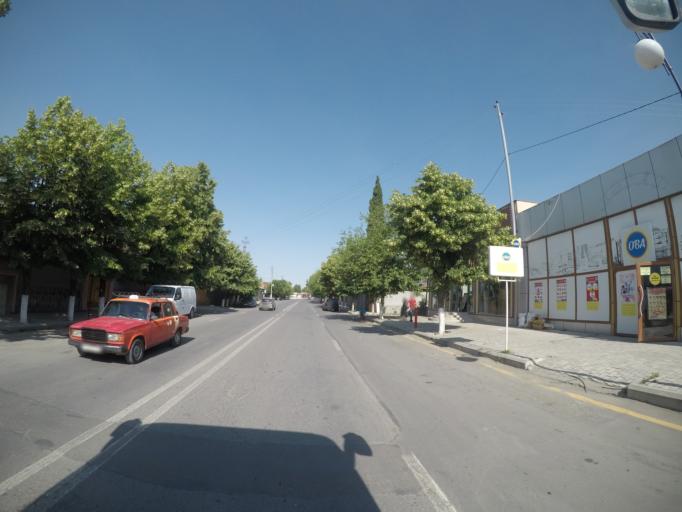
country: AZ
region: Shaki City
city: Sheki
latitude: 41.2061
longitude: 47.1718
